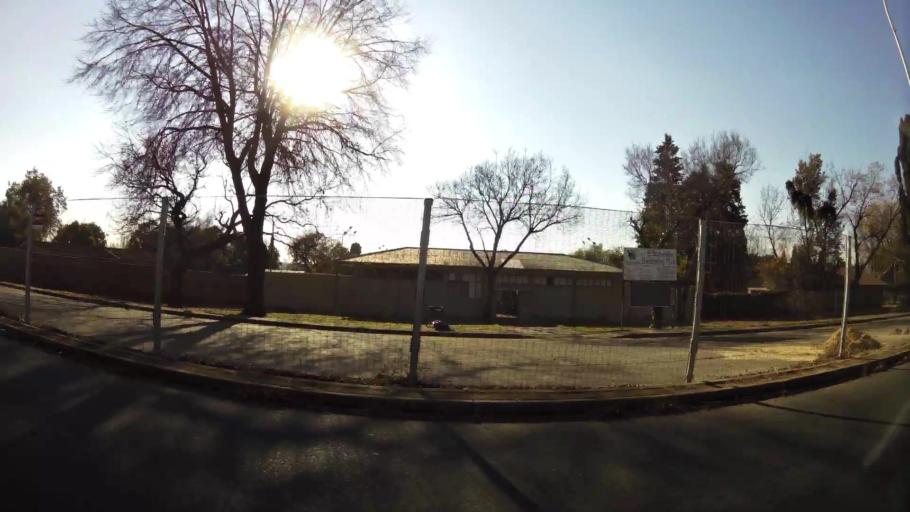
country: ZA
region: Gauteng
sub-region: City of Johannesburg Metropolitan Municipality
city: Modderfontein
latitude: -26.1443
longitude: 28.1618
